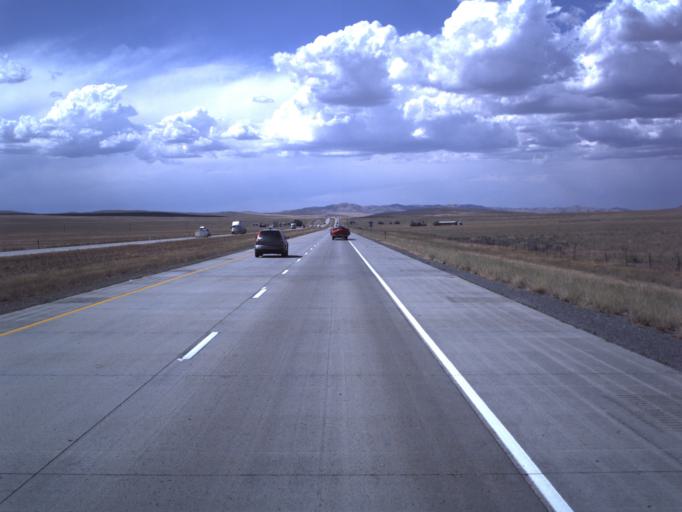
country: US
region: Utah
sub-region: Box Elder County
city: Garland
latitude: 41.8482
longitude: -112.4436
